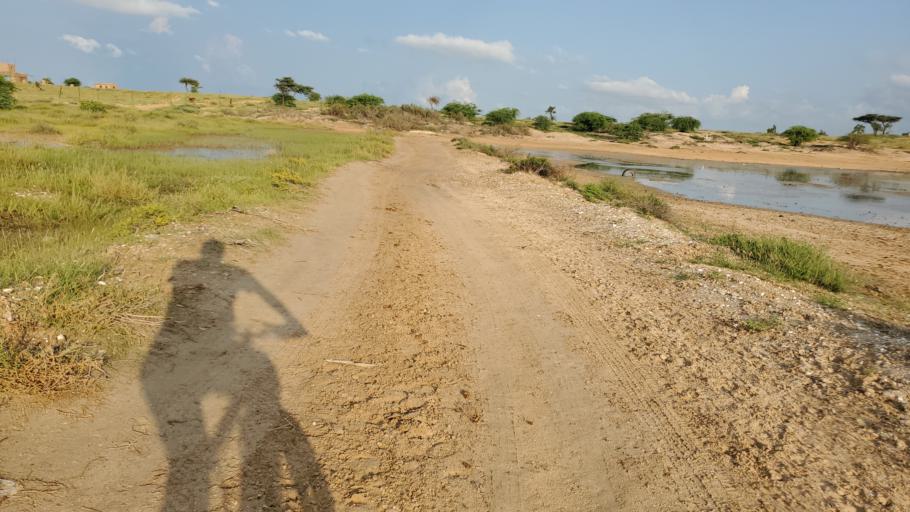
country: SN
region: Saint-Louis
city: Saint-Louis
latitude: 16.0488
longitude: -16.4171
